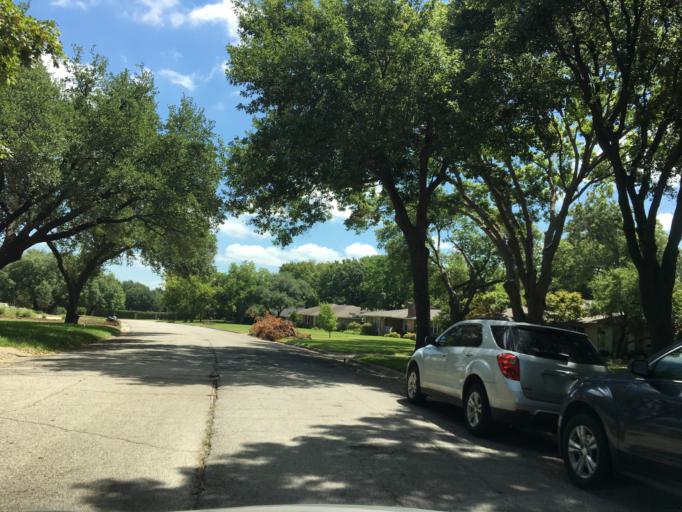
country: US
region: Texas
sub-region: Dallas County
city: Garland
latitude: 32.8391
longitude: -96.6531
